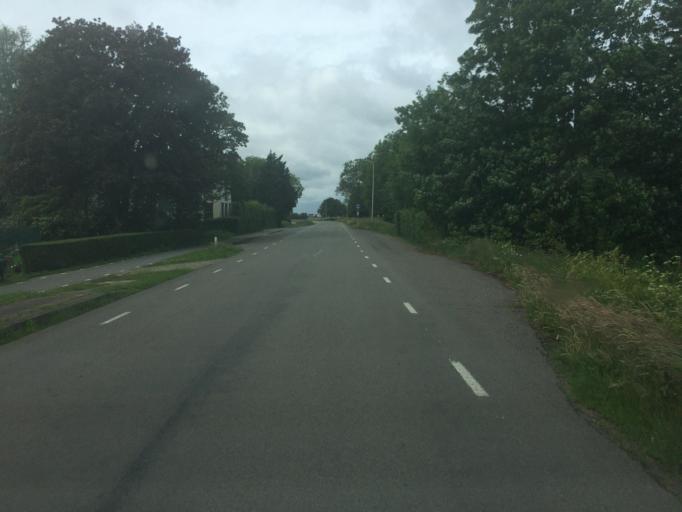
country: NL
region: Friesland
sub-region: Gemeente Lemsterland
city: Echtenerbrug
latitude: 52.8847
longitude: 5.8396
